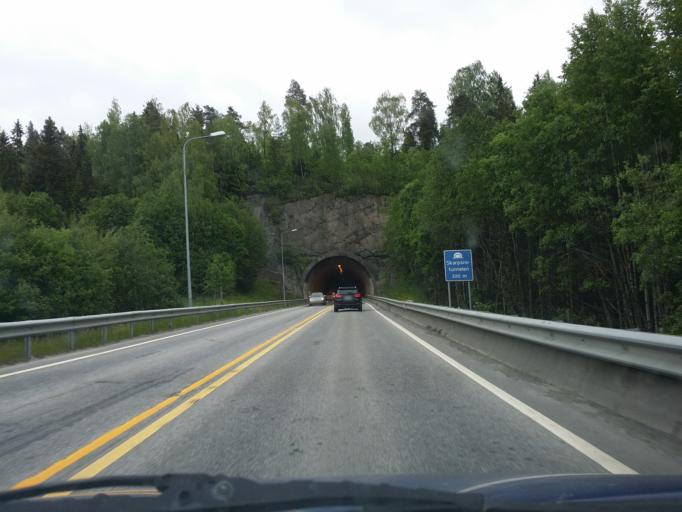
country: NO
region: Hedmark
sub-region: Ringsaker
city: Moelv
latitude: 60.9146
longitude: 10.7159
